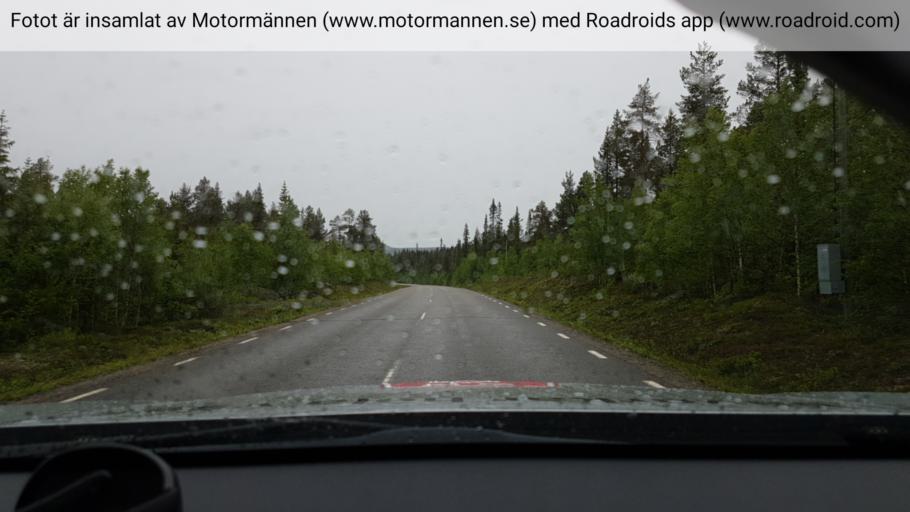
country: SE
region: Vaesterbotten
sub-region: Storumans Kommun
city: Fristad
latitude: 65.8444
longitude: 16.5887
